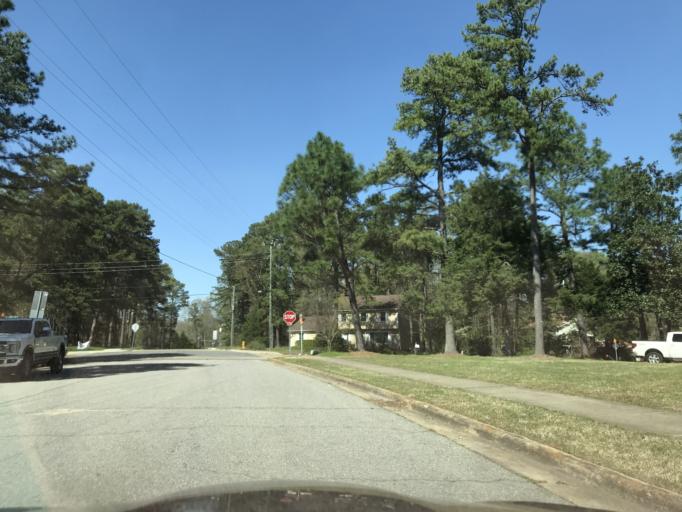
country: US
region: North Carolina
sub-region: Wake County
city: West Raleigh
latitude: 35.7767
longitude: -78.7034
